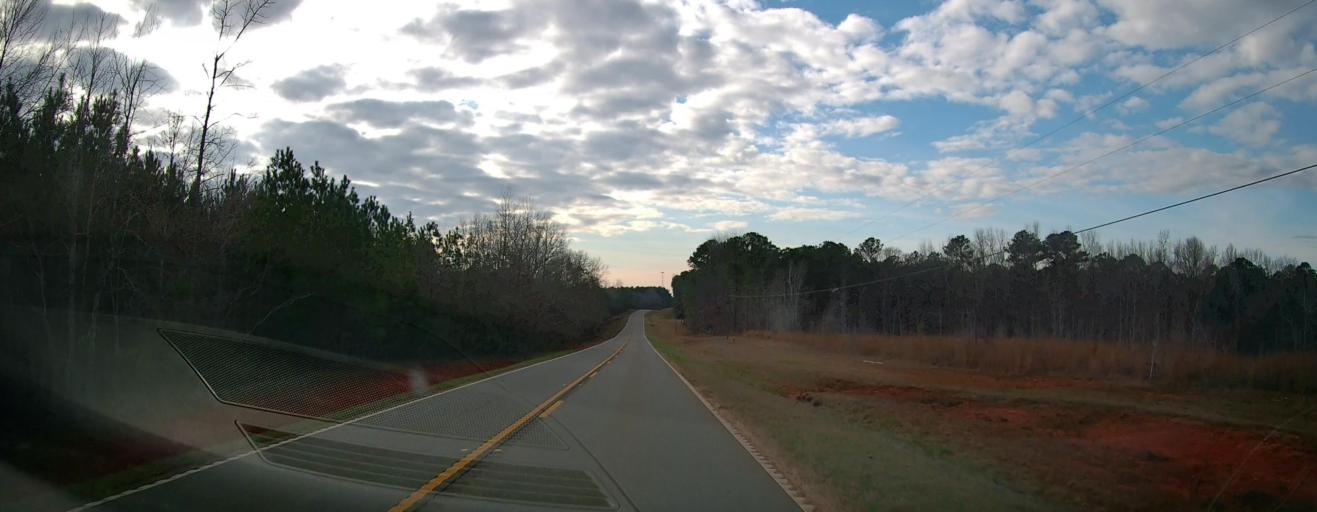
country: US
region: Georgia
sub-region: Harris County
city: Hamilton
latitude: 32.6866
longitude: -84.7741
